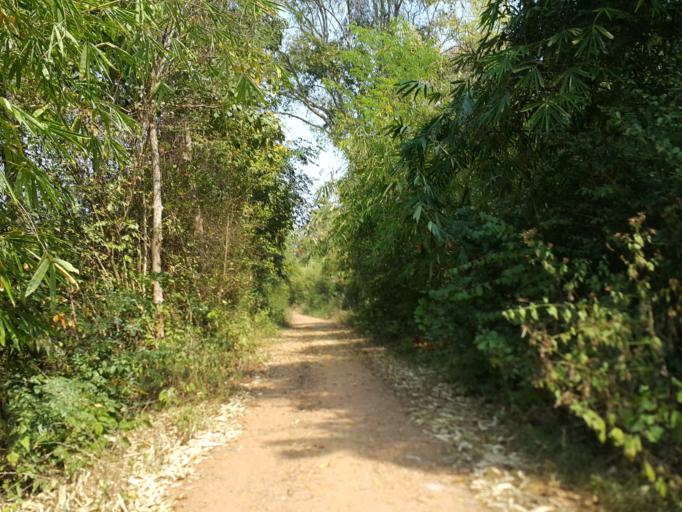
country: TH
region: Sukhothai
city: Thung Saliam
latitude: 17.3000
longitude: 99.5001
